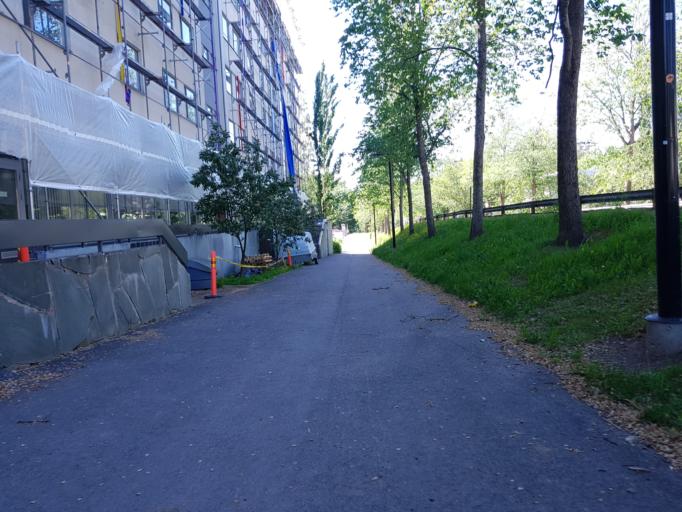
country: FI
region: Uusimaa
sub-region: Helsinki
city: Teekkarikylae
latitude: 60.2668
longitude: 24.8468
